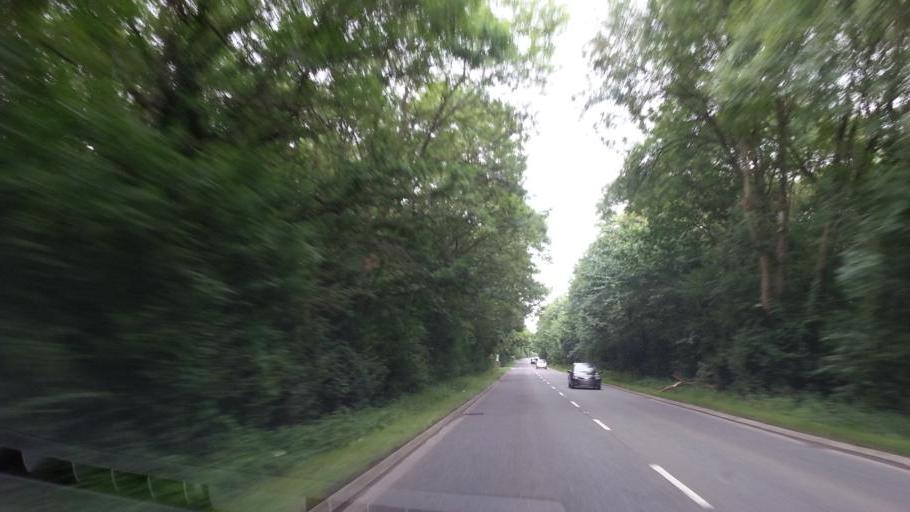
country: GB
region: England
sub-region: Wiltshire
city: North Bradley
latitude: 51.2855
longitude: -2.1856
